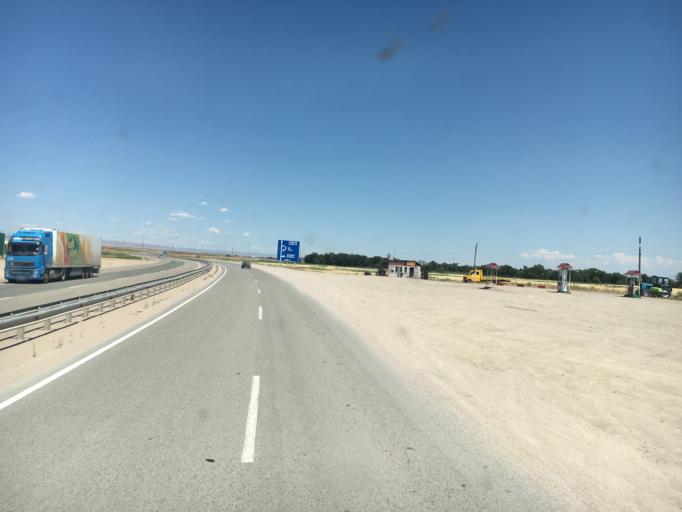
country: KG
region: Chuy
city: Sokuluk
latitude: 43.2691
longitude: 74.2229
